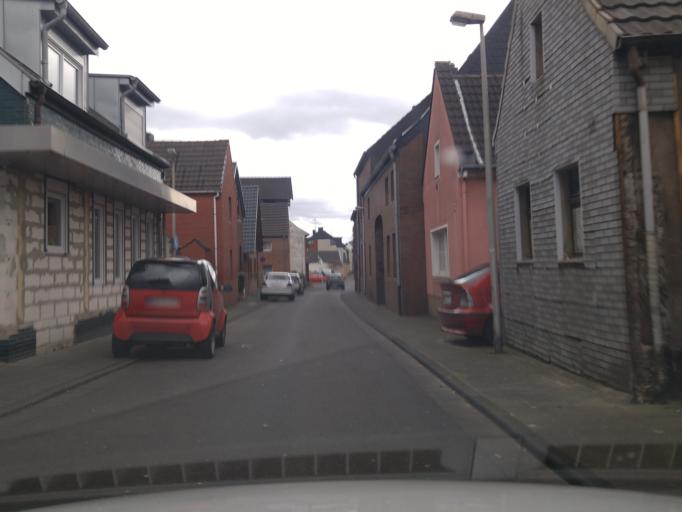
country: DE
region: North Rhine-Westphalia
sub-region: Regierungsbezirk Dusseldorf
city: Dormagen
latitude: 51.1406
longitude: 6.8163
